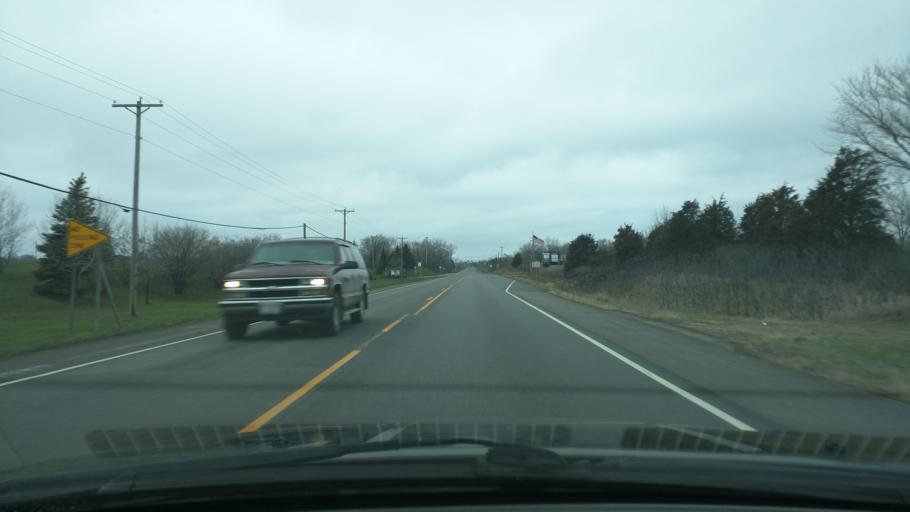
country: US
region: Minnesota
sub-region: Washington County
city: Saint Paul Park
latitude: 44.7531
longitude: -93.0063
